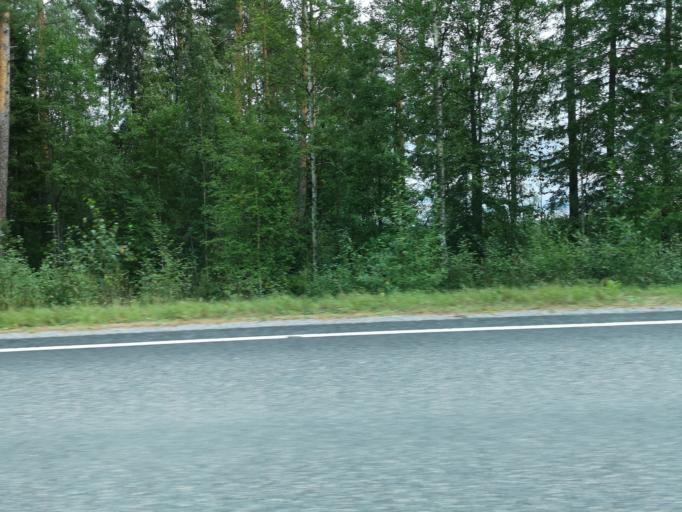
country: FI
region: Central Finland
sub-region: Jyvaeskylae
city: Hankasalmi
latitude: 62.3740
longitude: 26.4423
